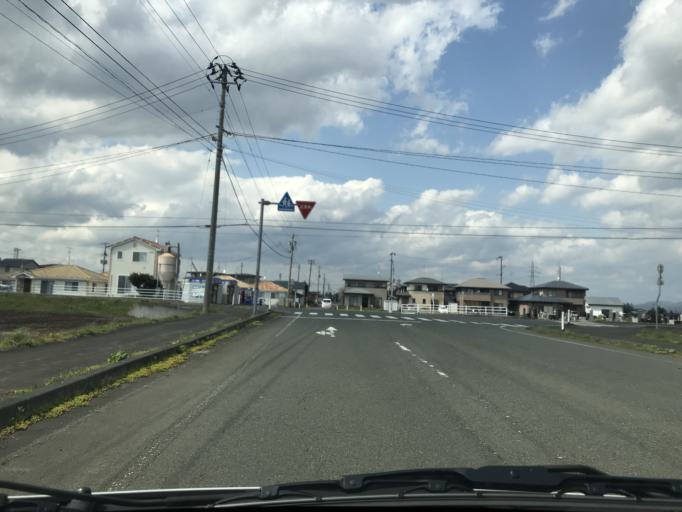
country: JP
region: Iwate
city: Mizusawa
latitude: 39.1632
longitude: 141.1214
